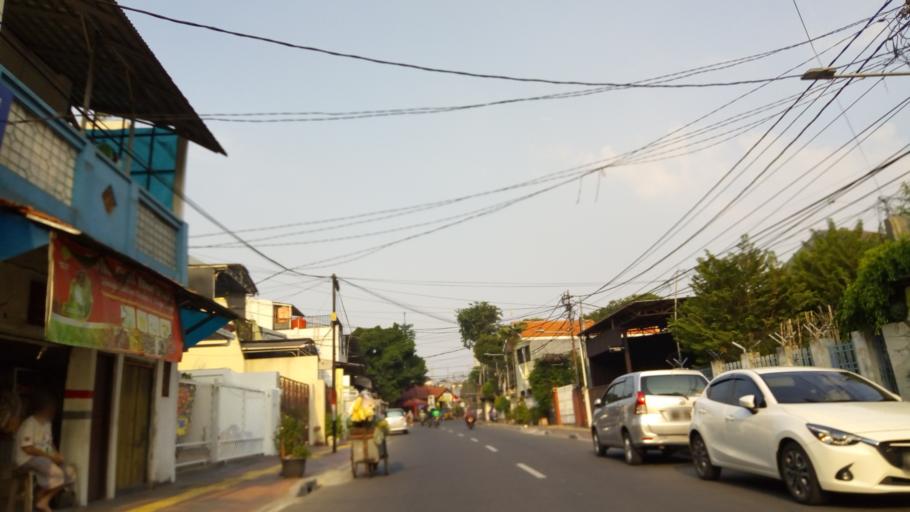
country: ID
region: Jakarta Raya
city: Jakarta
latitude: -6.1932
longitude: 106.8552
